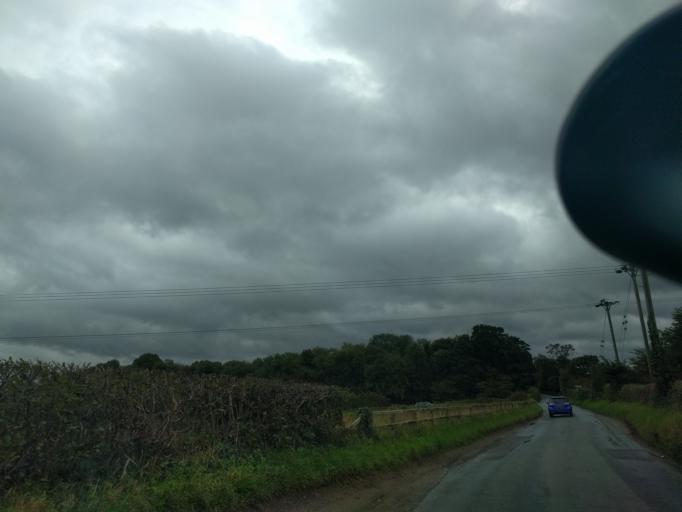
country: GB
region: England
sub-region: North Yorkshire
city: Bedale
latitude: 54.3246
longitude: -1.5658
